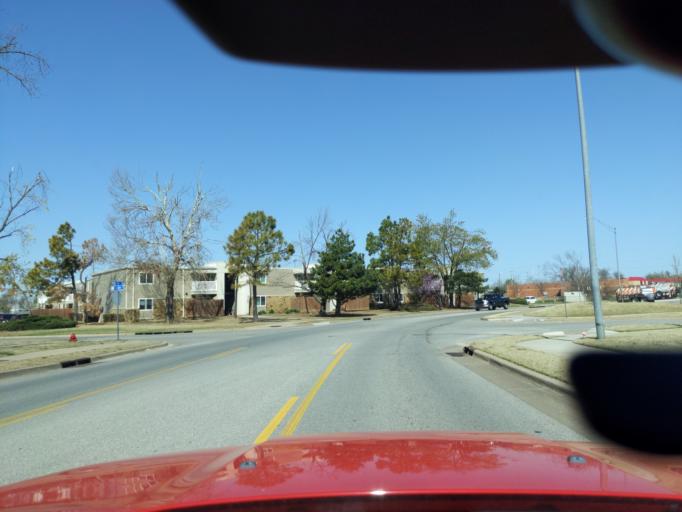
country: US
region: Oklahoma
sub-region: Cleveland County
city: Moore
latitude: 35.3466
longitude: -97.4986
